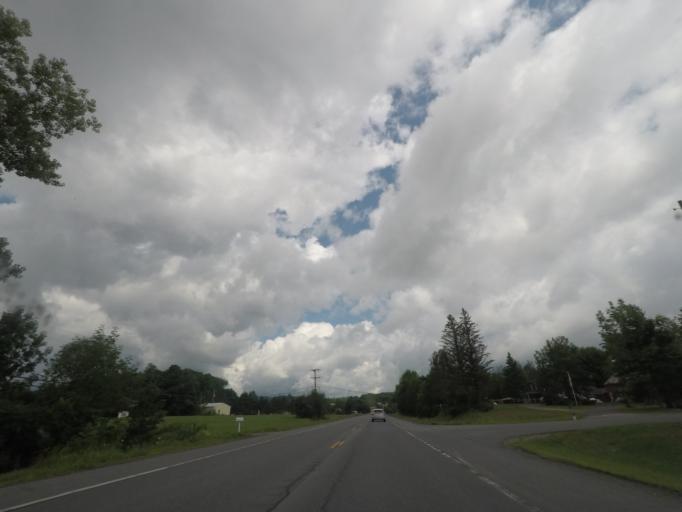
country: US
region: Massachusetts
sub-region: Berkshire County
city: Lanesborough
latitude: 42.5921
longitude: -73.3685
